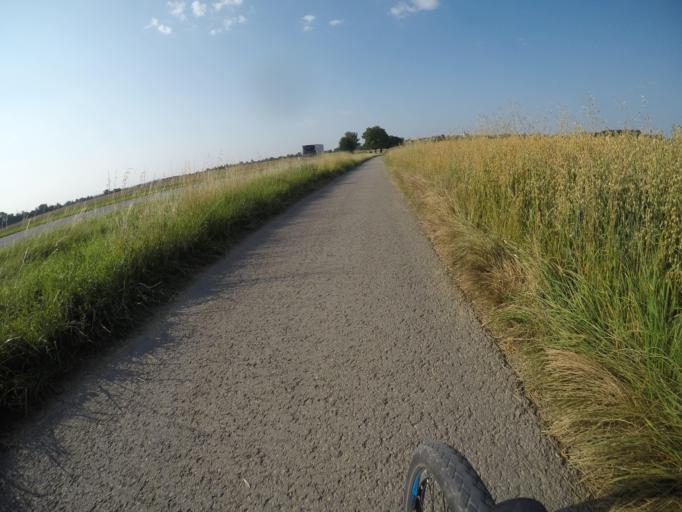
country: DE
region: Baden-Wuerttemberg
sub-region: Regierungsbezirk Stuttgart
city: Herrenberg
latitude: 48.5619
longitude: 8.8800
